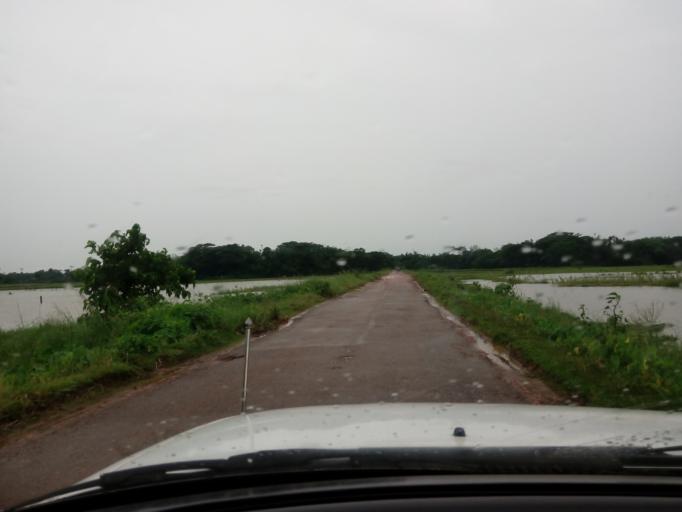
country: BD
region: Sylhet
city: Sylhet
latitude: 24.9623
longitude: 91.7955
